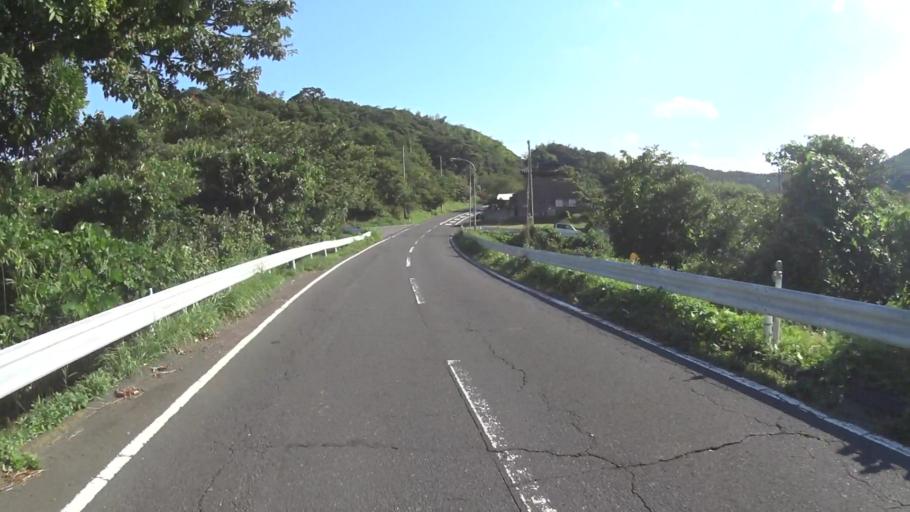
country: JP
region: Kyoto
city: Miyazu
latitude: 35.7117
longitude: 135.0692
